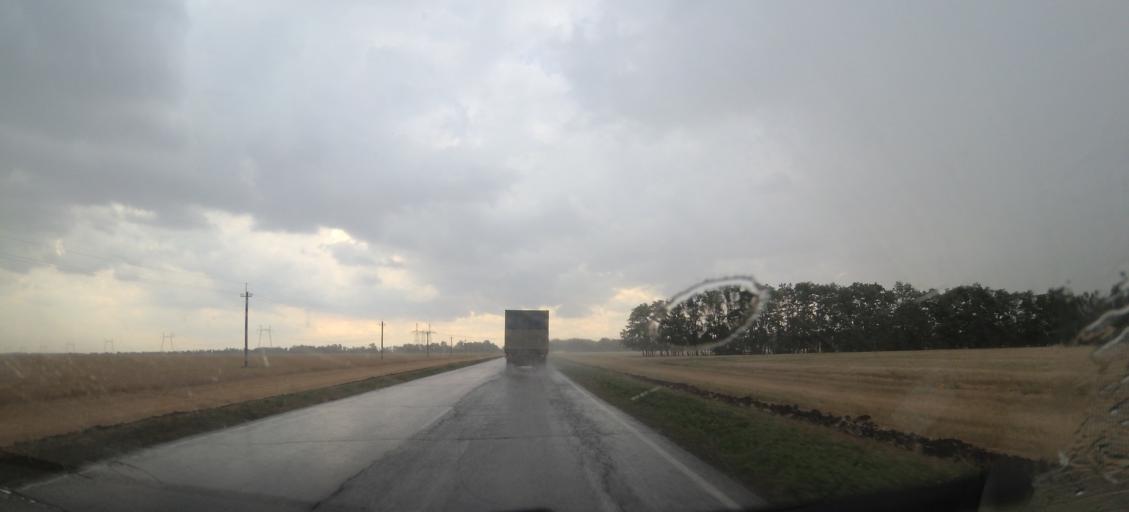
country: RU
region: Rostov
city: Gundorovskiy
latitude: 46.8609
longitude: 41.9488
